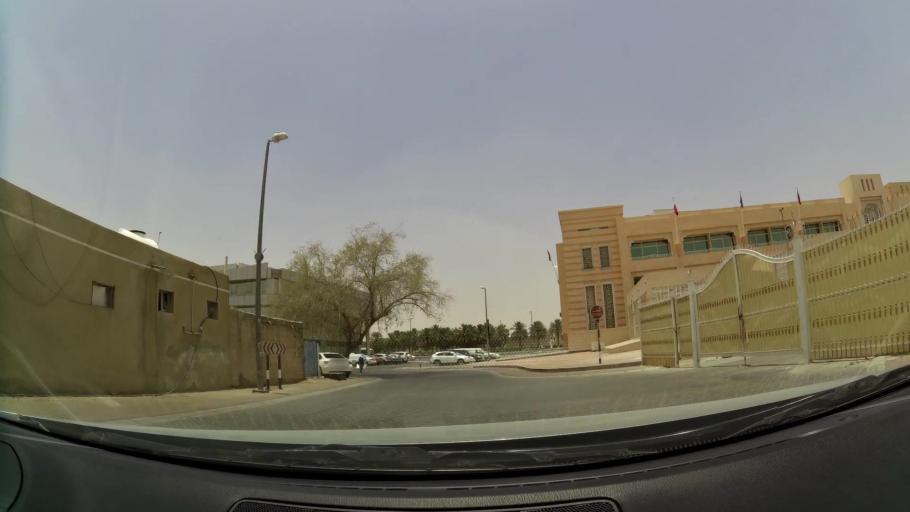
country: AE
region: Abu Dhabi
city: Al Ain
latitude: 24.2230
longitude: 55.7278
